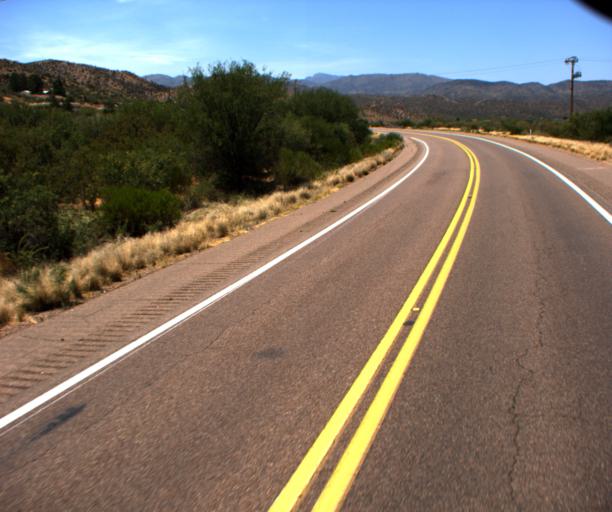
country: US
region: Arizona
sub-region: Gila County
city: Tonto Basin
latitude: 33.9456
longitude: -111.3172
